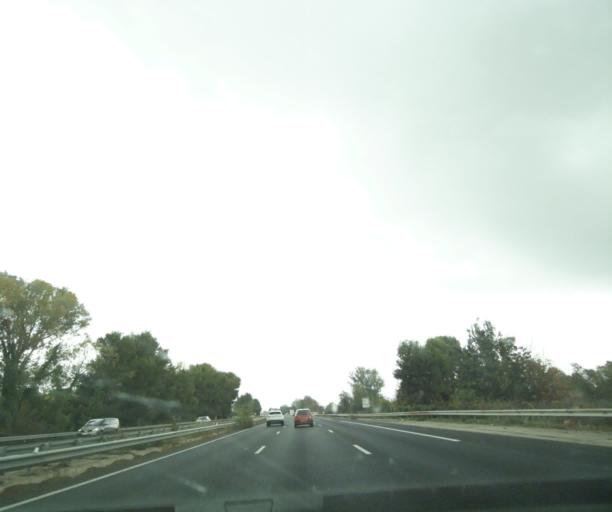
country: FR
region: Languedoc-Roussillon
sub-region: Departement de l'Herault
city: Sauvian
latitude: 43.3110
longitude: 3.2516
